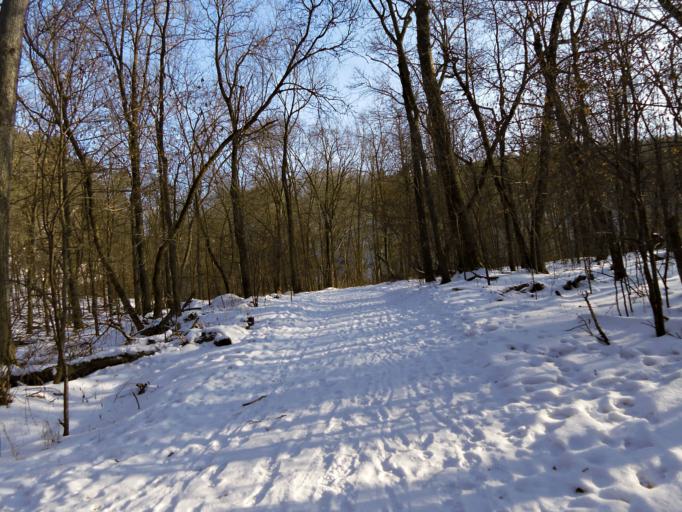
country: US
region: Wisconsin
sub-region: Saint Croix County
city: North Hudson
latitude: 45.0209
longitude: -92.6763
